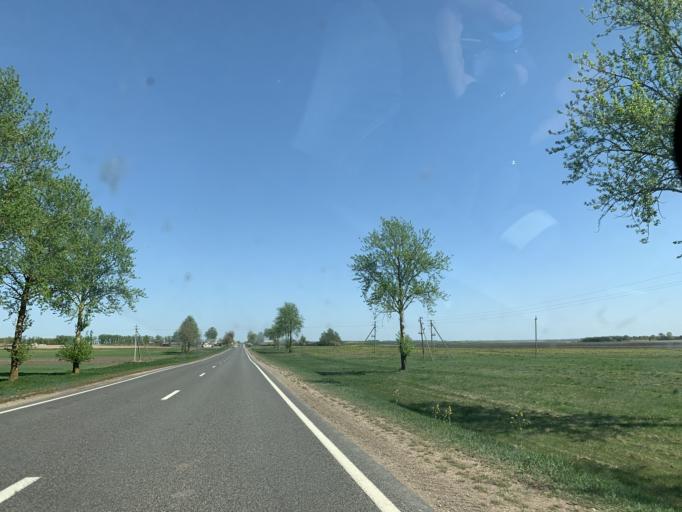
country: BY
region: Minsk
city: Nyasvizh
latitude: 53.2346
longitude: 26.8136
